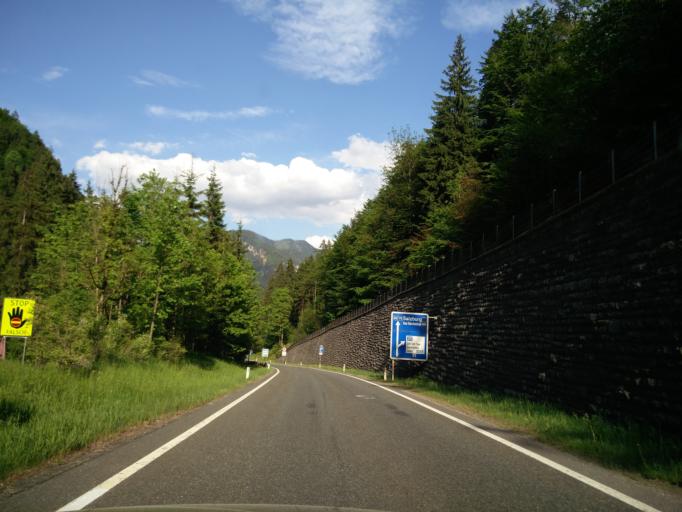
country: AT
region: Salzburg
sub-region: Politischer Bezirk Zell am See
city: Lofer
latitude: 47.5785
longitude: 12.6674
